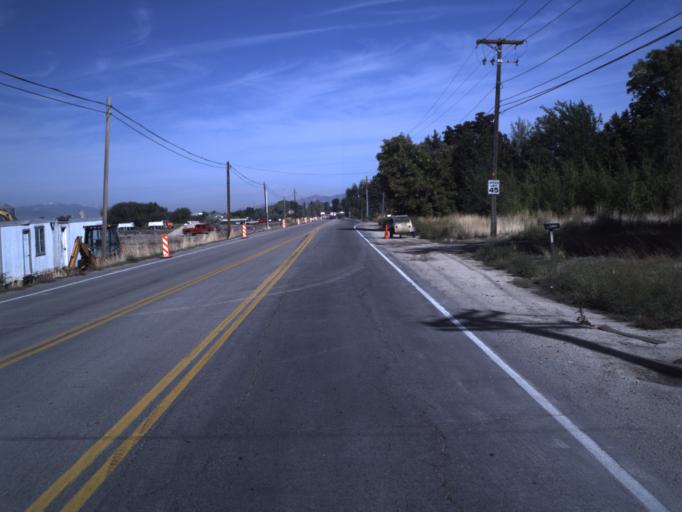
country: US
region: Utah
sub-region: Utah County
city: Orem
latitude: 40.2608
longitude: -111.7163
